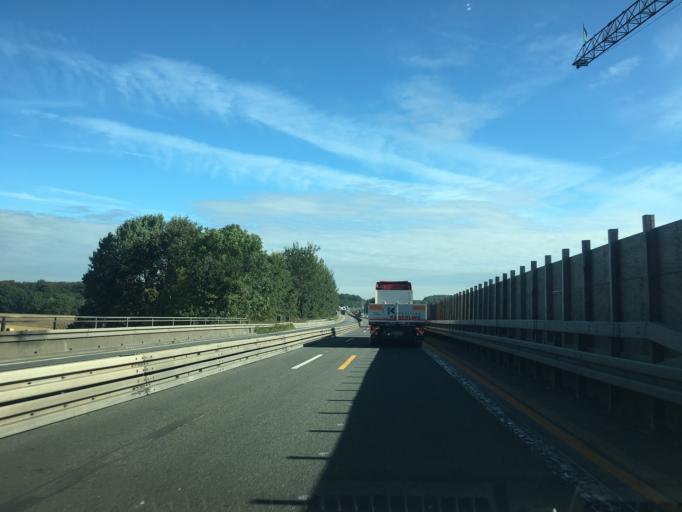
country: DE
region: North Rhine-Westphalia
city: Lengerich
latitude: 52.2233
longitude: 7.8727
